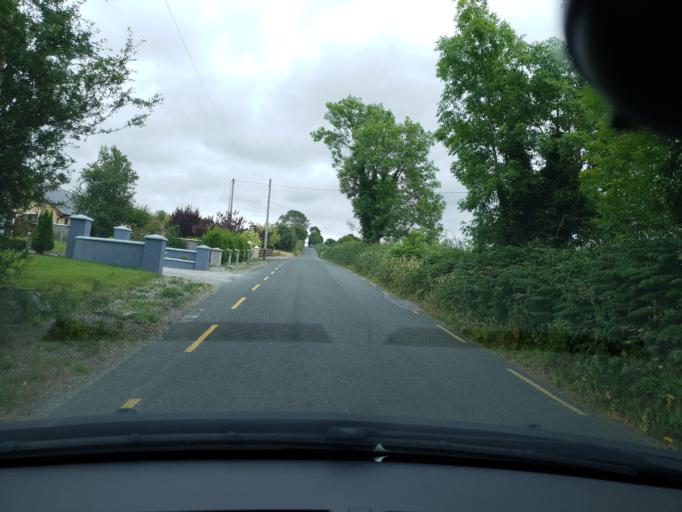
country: IE
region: Munster
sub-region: Ciarrai
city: Cill Airne
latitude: 52.1503
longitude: -9.5953
